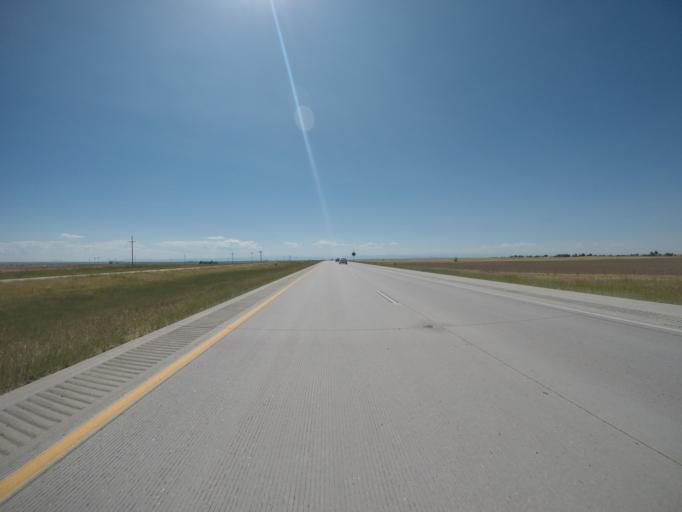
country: US
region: Colorado
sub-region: Adams County
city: Bennett
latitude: 39.7396
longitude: -104.5607
